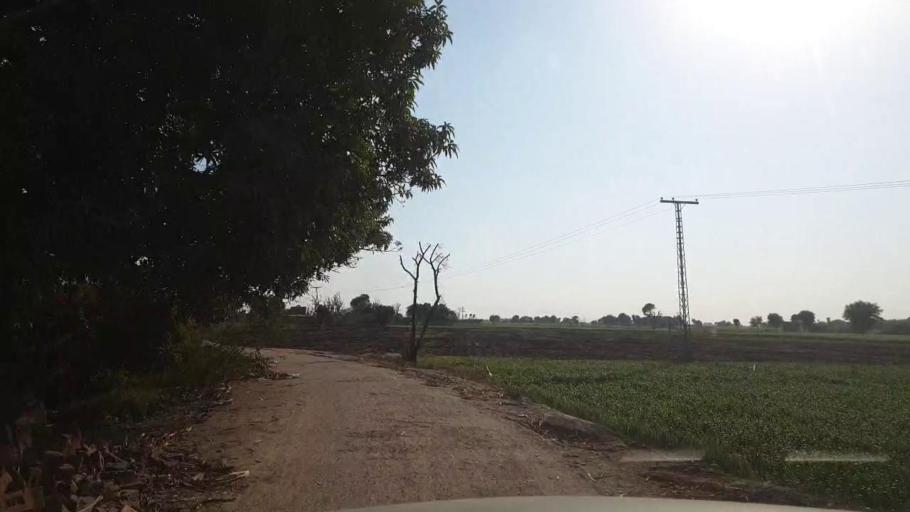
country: PK
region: Sindh
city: Tando Adam
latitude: 25.6864
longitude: 68.6882
